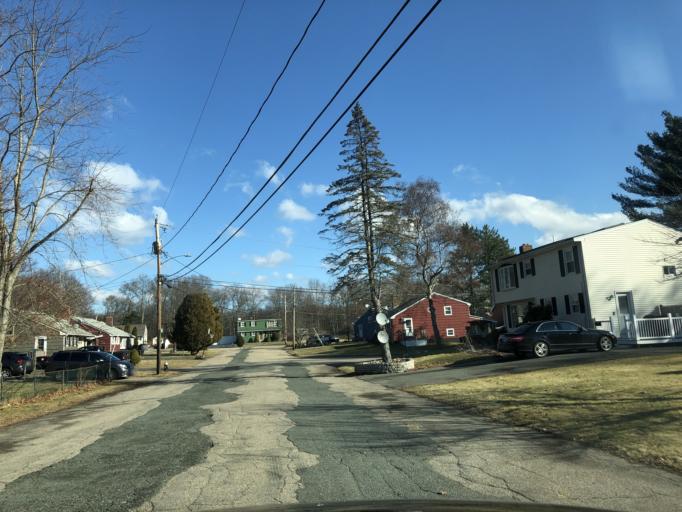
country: US
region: Massachusetts
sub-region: Norfolk County
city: Avon
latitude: 42.1144
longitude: -71.0146
